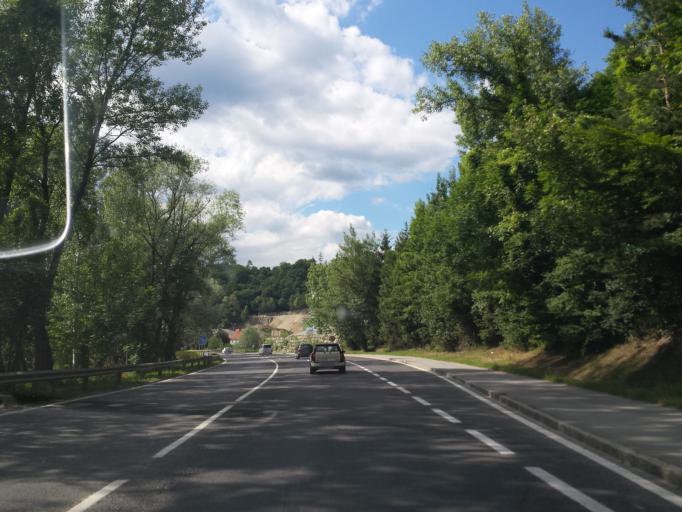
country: AT
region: Styria
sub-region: Politischer Bezirk Graz-Umgebung
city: Gratkorn
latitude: 47.1186
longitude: 15.3747
